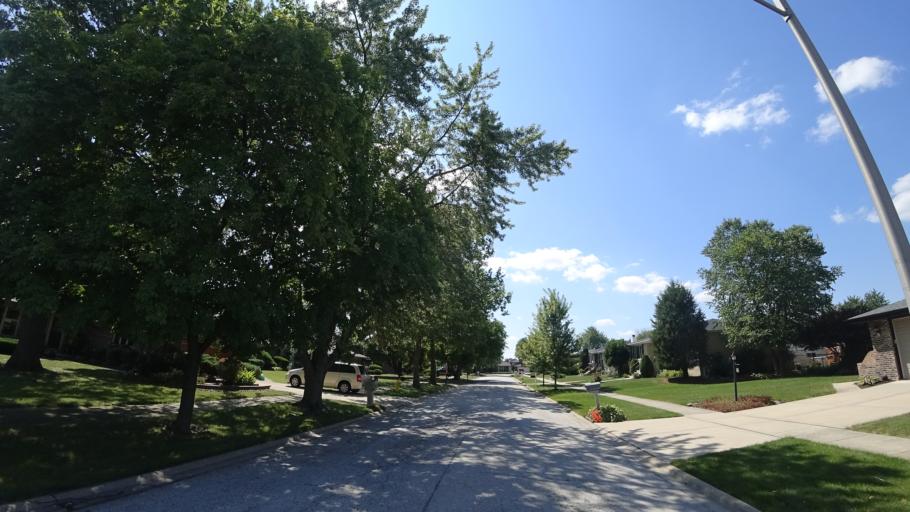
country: US
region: Illinois
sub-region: Cook County
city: Orland Park
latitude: 41.6326
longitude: -87.8394
